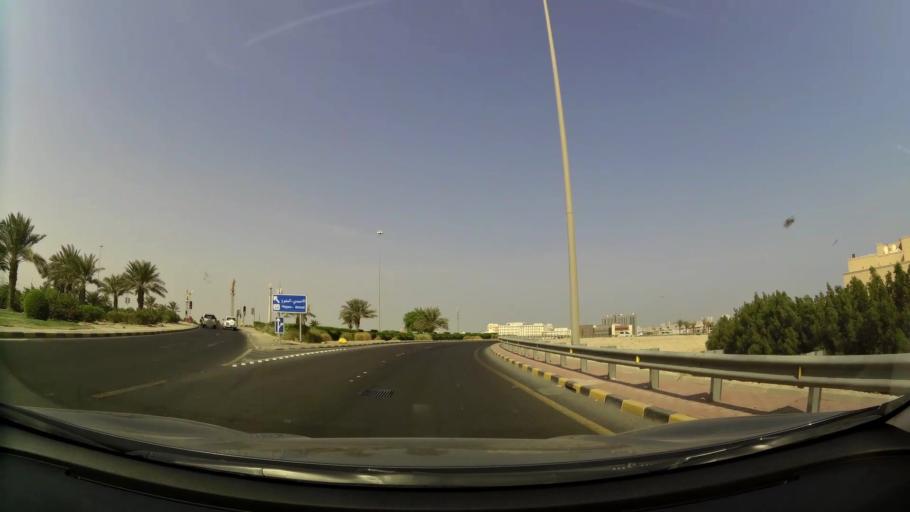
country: KW
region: Al Ahmadi
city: Ar Riqqah
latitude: 29.1304
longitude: 48.0927
